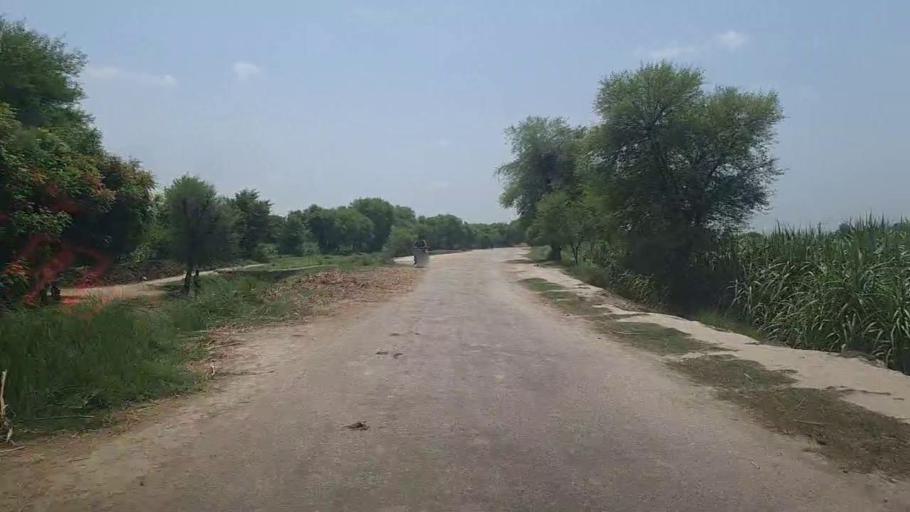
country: PK
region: Sindh
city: Ubauro
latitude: 28.2848
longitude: 69.8089
